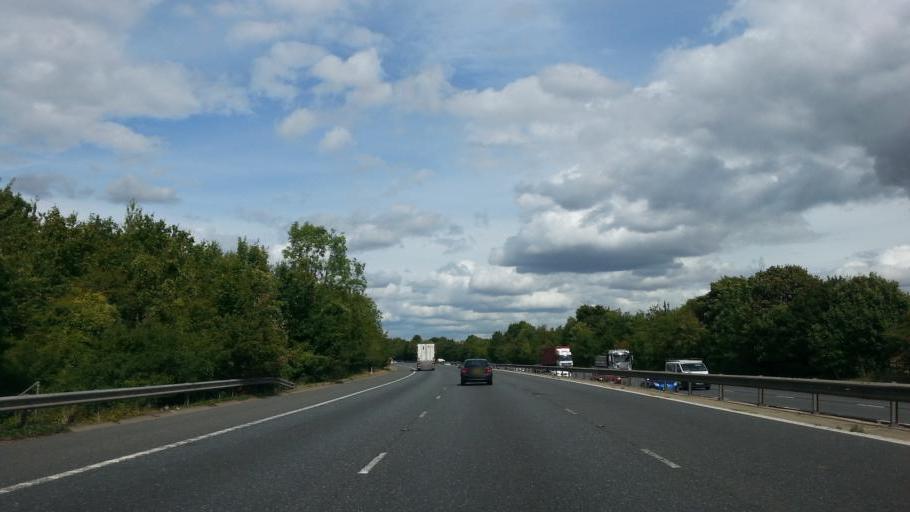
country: GB
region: England
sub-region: Essex
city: Little Hallingbury
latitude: 51.8297
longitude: 0.1906
